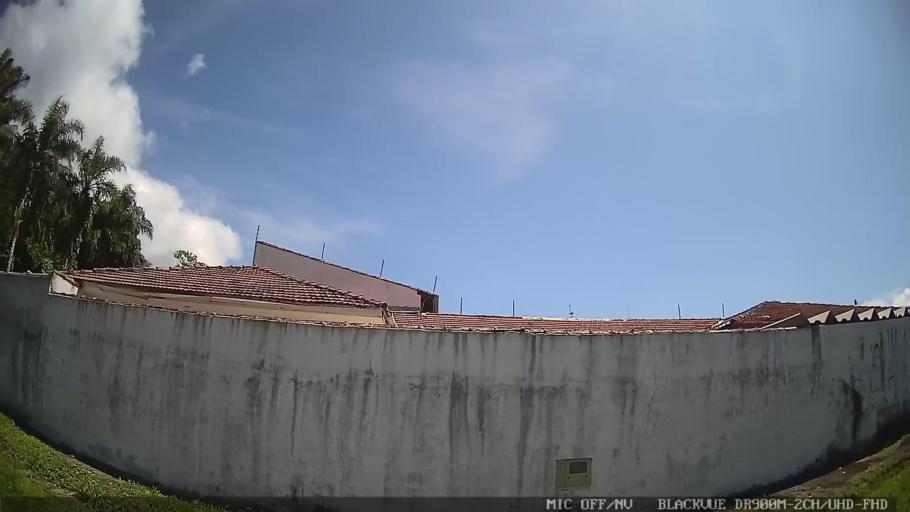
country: BR
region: Sao Paulo
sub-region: Peruibe
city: Peruibe
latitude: -24.3342
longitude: -47.0049
